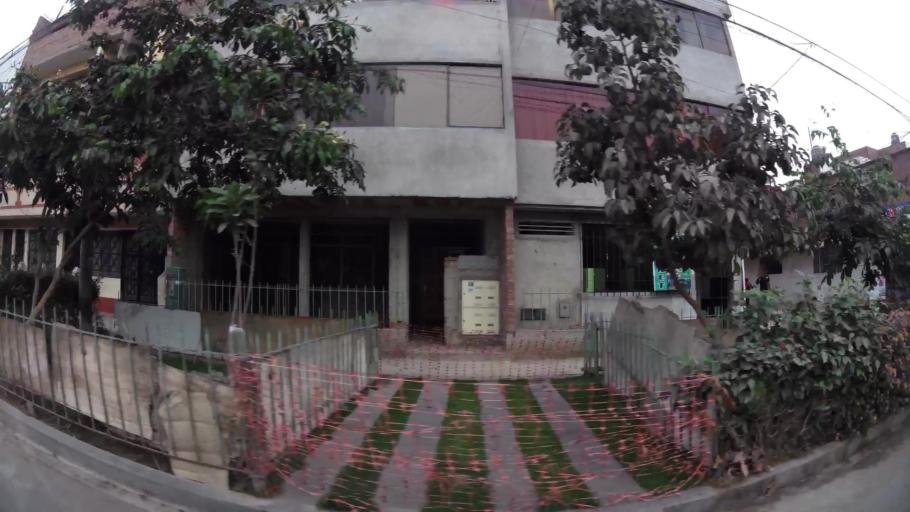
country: PE
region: Lima
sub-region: Lima
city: Independencia
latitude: -11.9933
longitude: -77.0069
